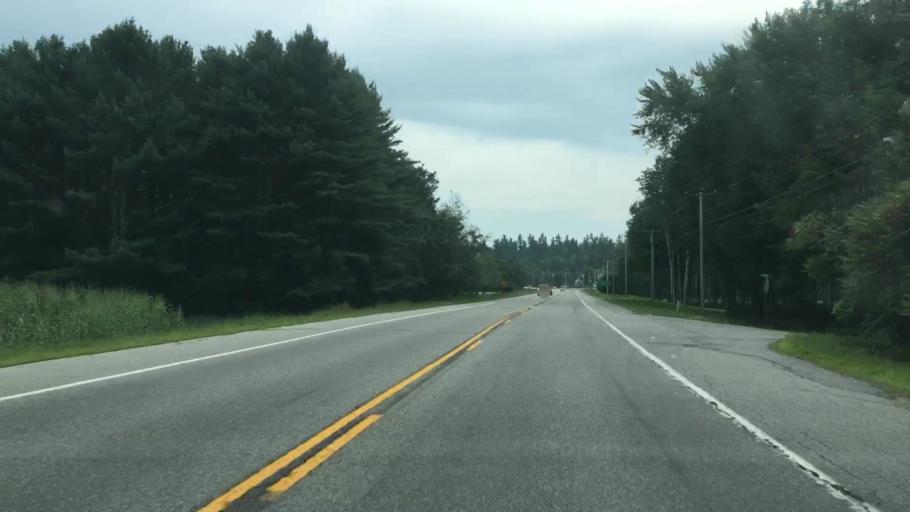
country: US
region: Maine
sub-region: Oxford County
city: Bethel
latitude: 44.4537
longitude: -70.8058
